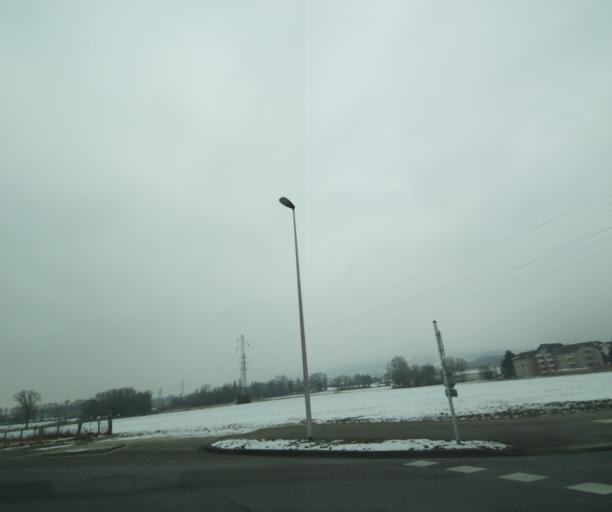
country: FR
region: Rhone-Alpes
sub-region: Departement de la Haute-Savoie
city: Reignier-Esery
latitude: 46.1357
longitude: 6.2759
